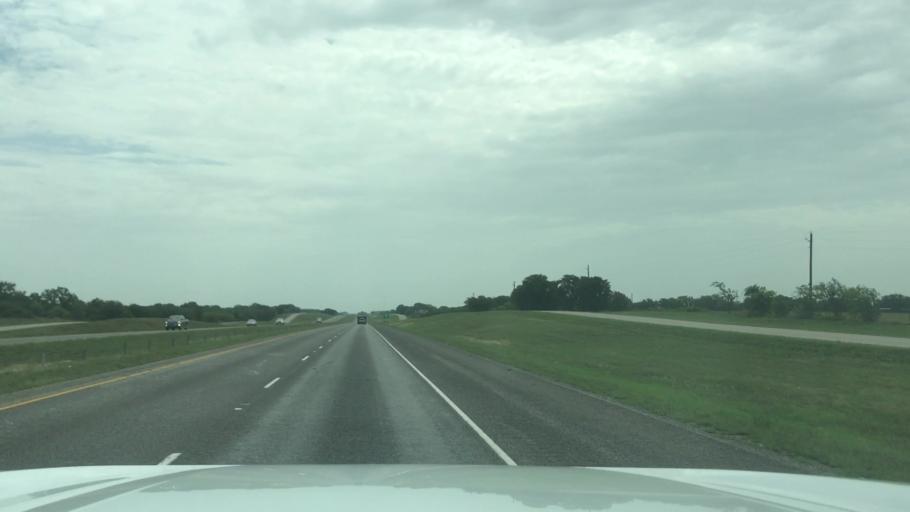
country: US
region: Texas
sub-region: Eastland County
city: Cisco
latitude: 32.3754
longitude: -98.9161
